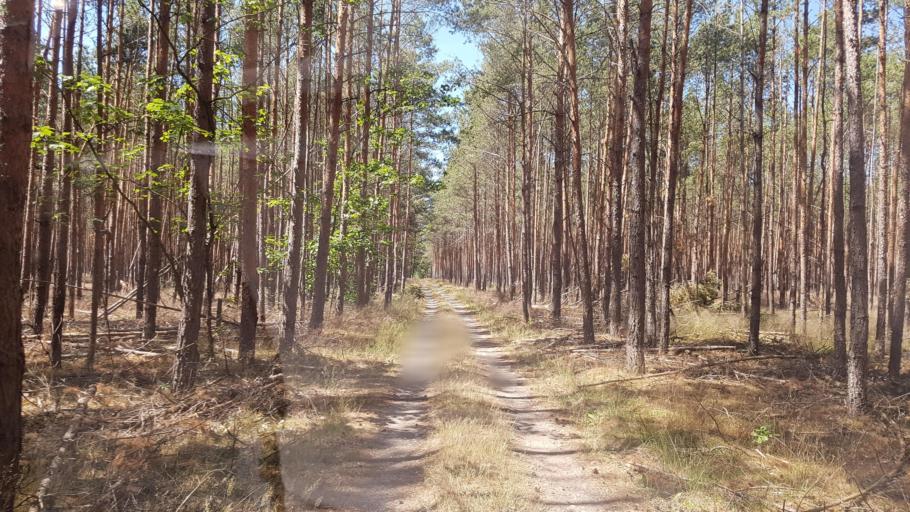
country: DE
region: Brandenburg
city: Treuenbrietzen
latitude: 52.0470
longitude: 12.8396
